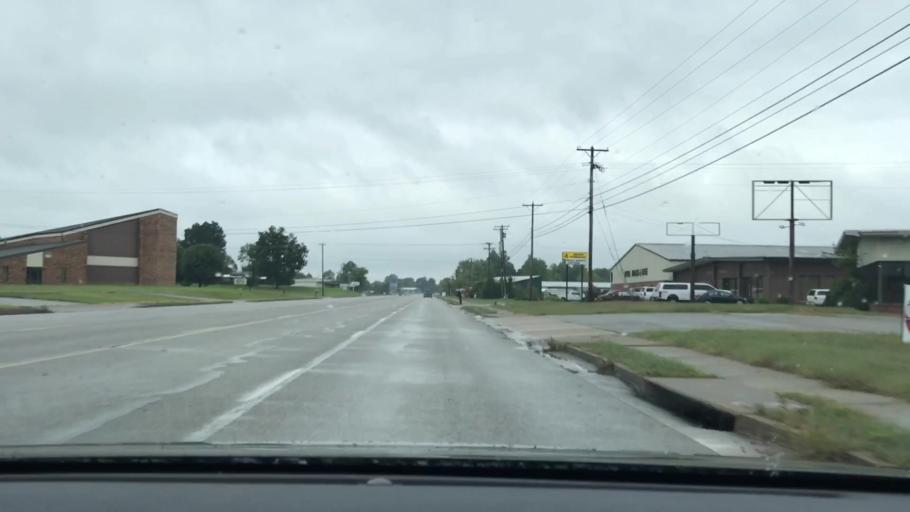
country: US
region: Kentucky
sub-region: Hopkins County
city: Madisonville
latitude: 37.3276
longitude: -87.4460
